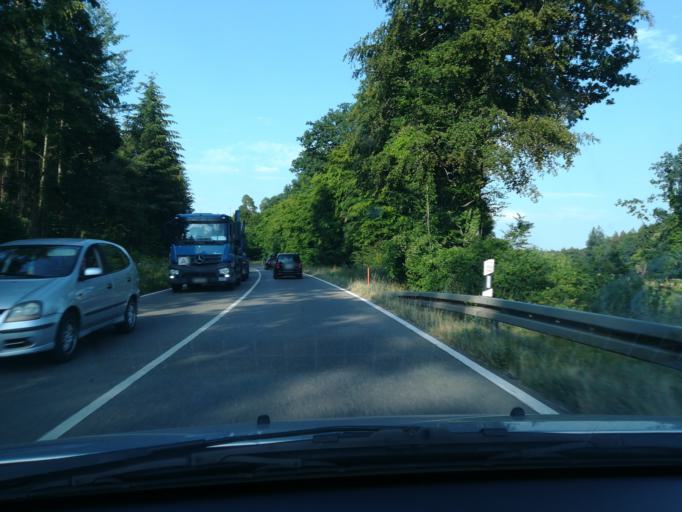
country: DE
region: Baden-Wuerttemberg
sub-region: Freiburg Region
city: Gottmadingen
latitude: 47.7389
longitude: 8.8076
